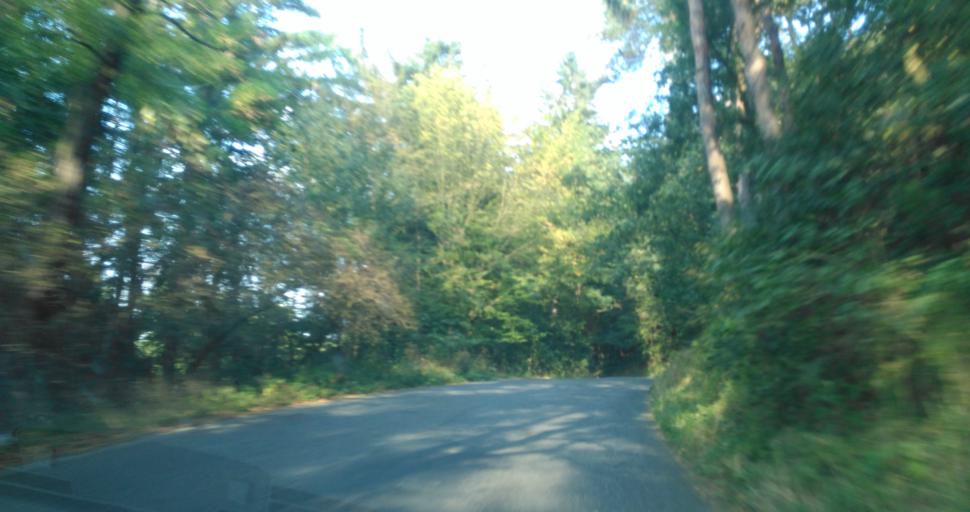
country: CZ
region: Central Bohemia
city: Zebrak
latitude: 49.8925
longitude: 13.8855
